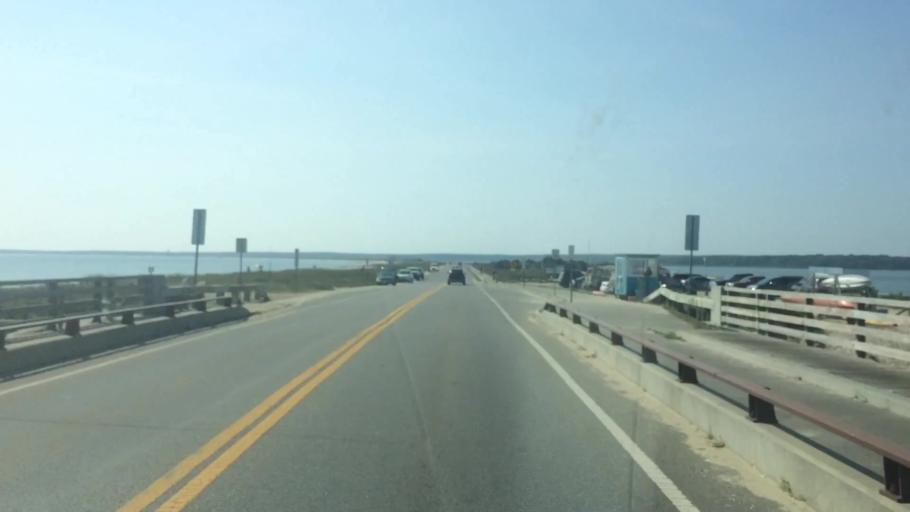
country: US
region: Massachusetts
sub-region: Dukes County
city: Oak Bluffs
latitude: 41.4336
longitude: -70.5567
